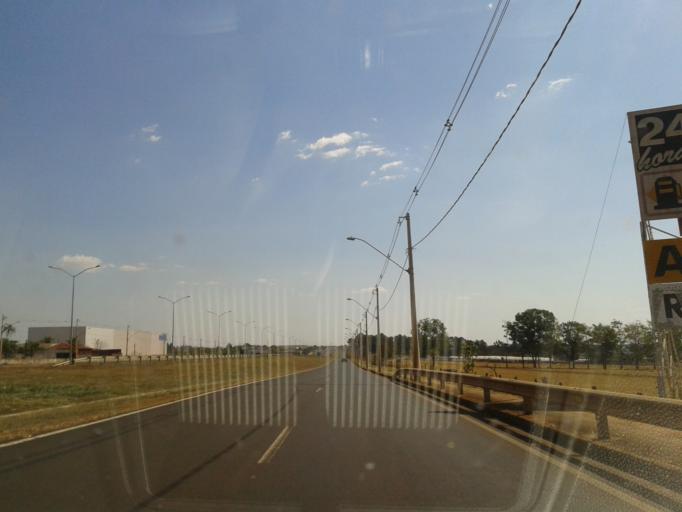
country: BR
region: Minas Gerais
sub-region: Araguari
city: Araguari
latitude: -18.6569
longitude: -48.1534
